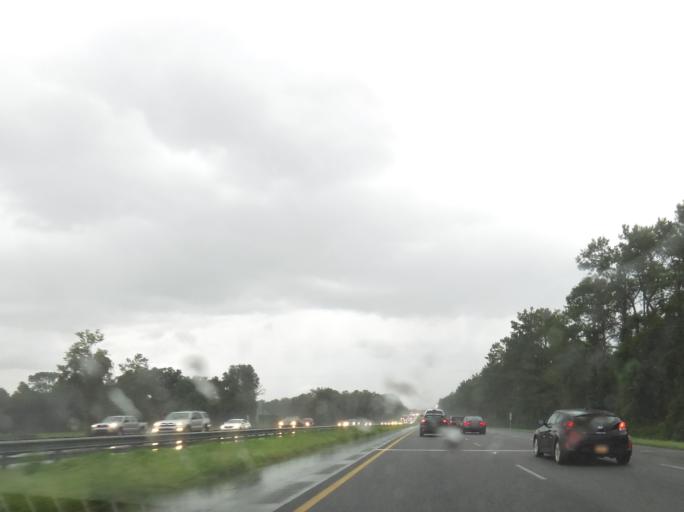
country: US
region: Florida
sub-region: Alachua County
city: High Springs
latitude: 29.9657
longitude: -82.5734
